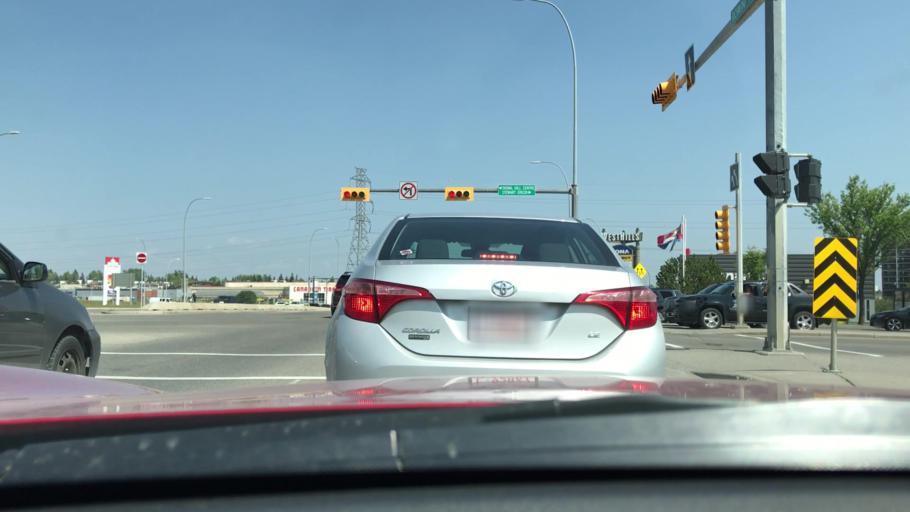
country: CA
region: Alberta
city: Calgary
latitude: 51.0177
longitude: -114.1684
